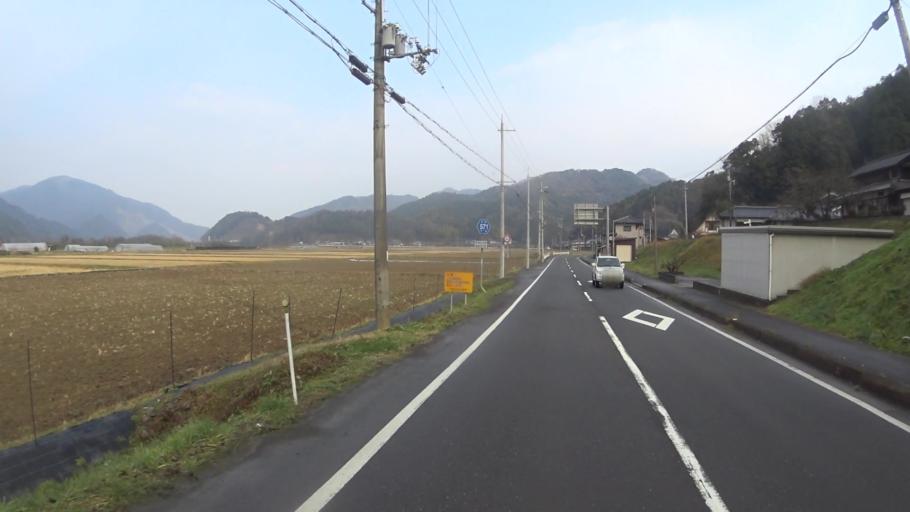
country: JP
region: Kyoto
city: Maizuru
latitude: 35.4563
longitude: 135.2840
